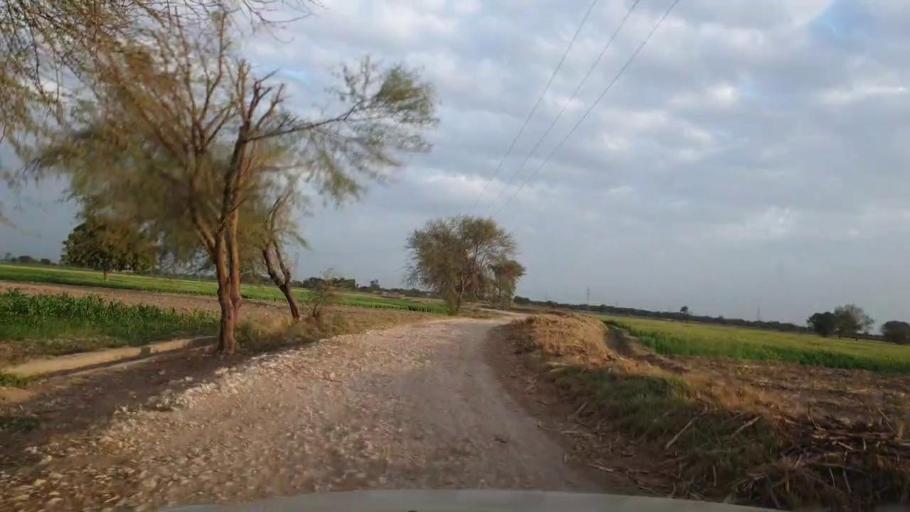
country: PK
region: Sindh
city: Matiari
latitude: 25.5690
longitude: 68.4417
